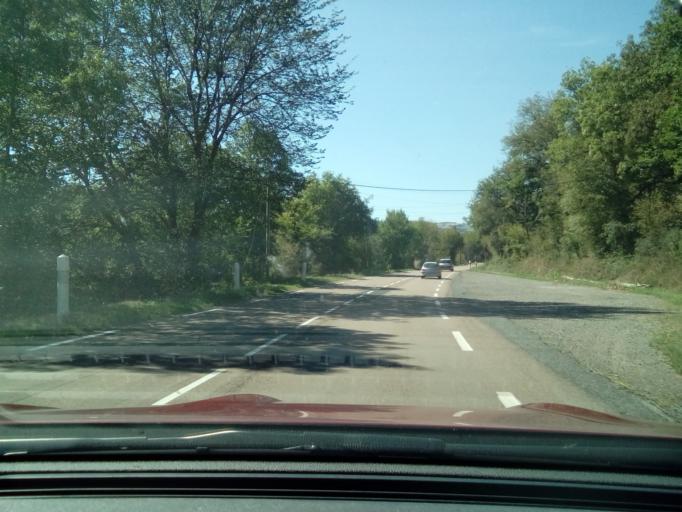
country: FR
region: Rhone-Alpes
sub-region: Departement du Rhone
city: Saint-Verand
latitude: 45.9029
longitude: 4.5361
